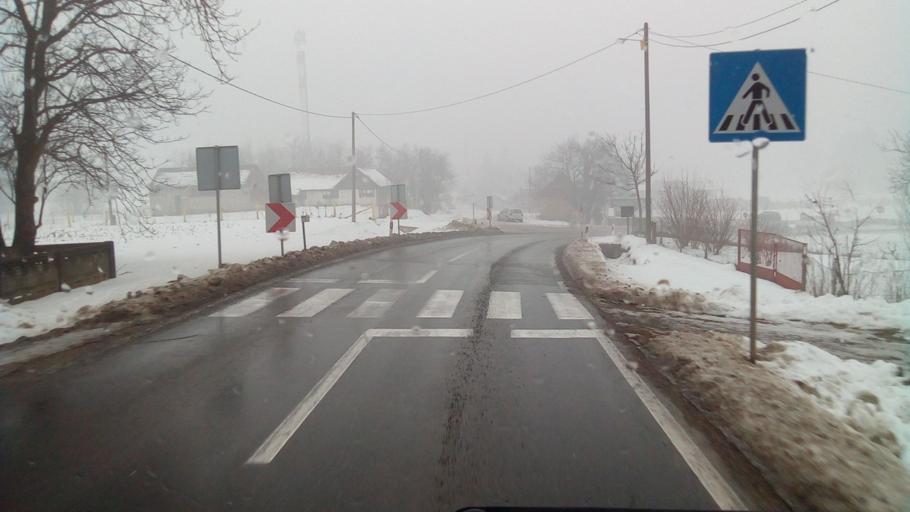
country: HR
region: Sisacko-Moslavacka
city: Petrinja
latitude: 45.5118
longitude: 16.2532
